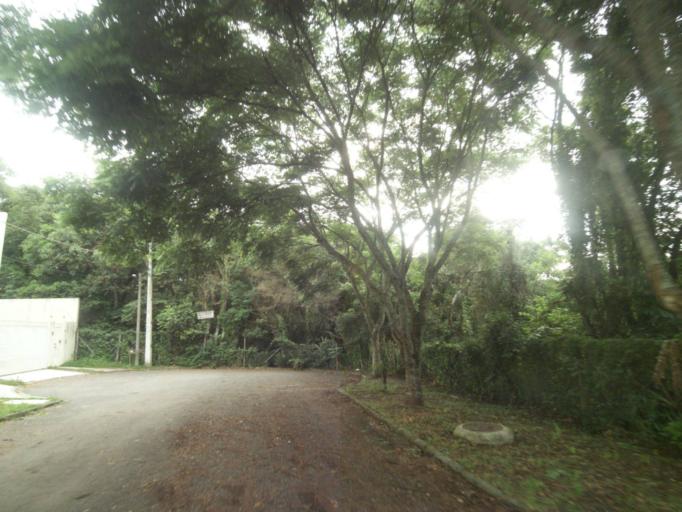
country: BR
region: Parana
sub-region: Curitiba
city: Curitiba
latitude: -25.3957
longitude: -49.2980
